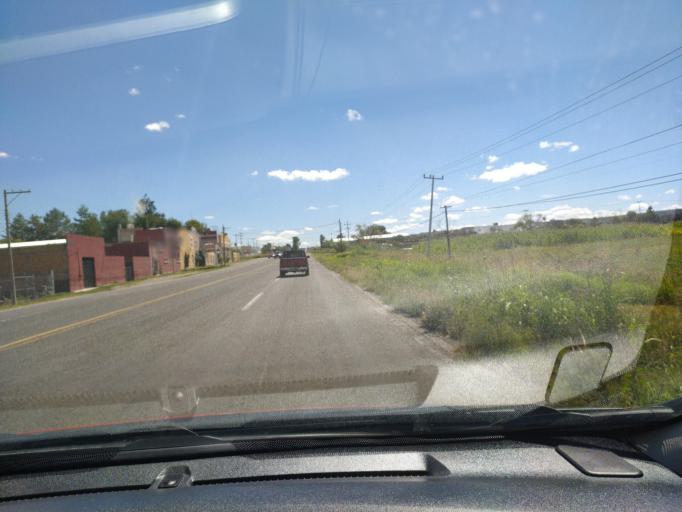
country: MX
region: Jalisco
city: San Miguel el Alto
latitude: 21.0265
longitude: -102.3772
